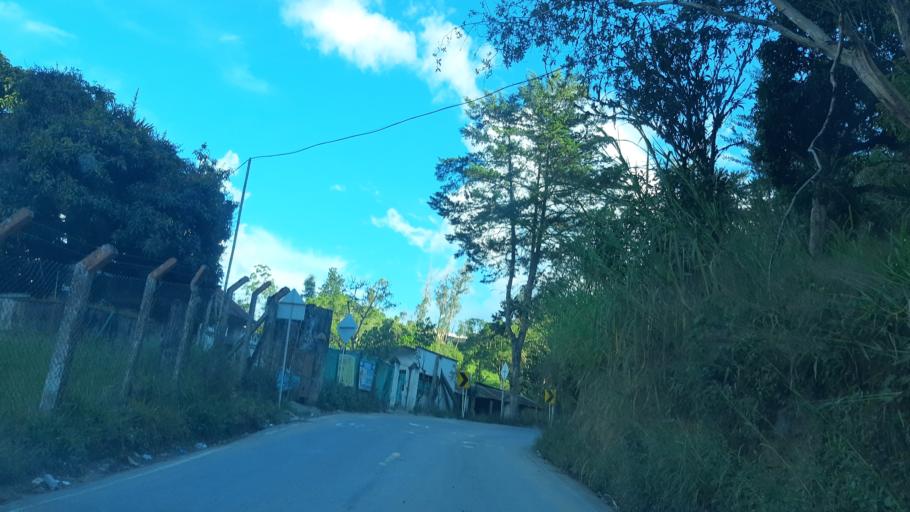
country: CO
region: Cundinamarca
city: Tenza
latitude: 5.0782
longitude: -73.3919
